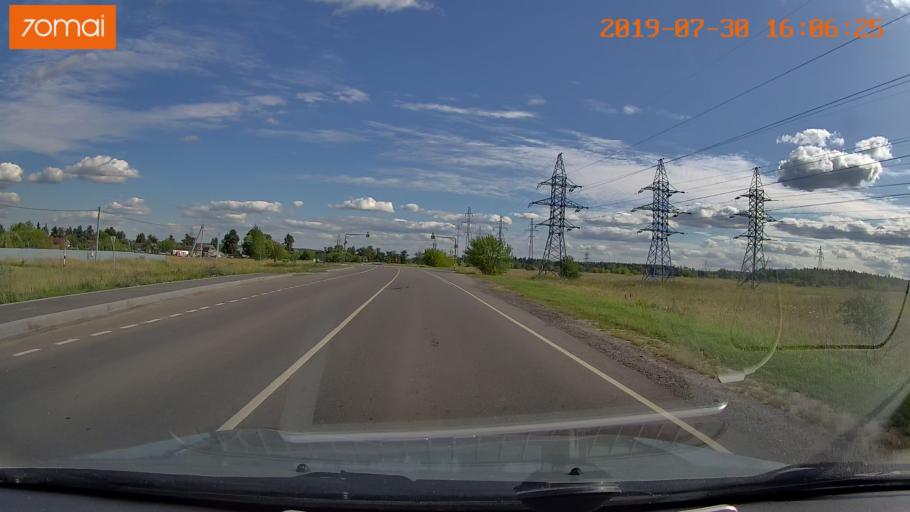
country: RU
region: Moskovskaya
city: Peski
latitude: 55.2561
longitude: 38.7164
